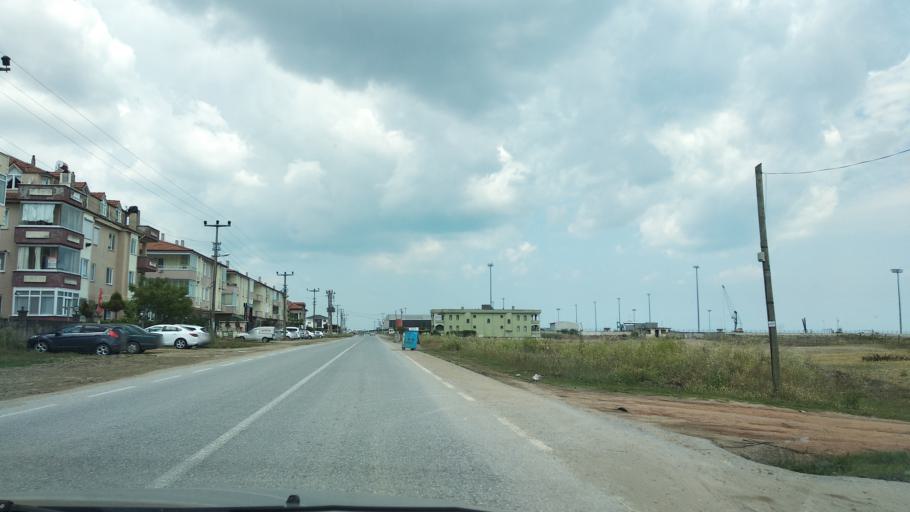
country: TR
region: Sakarya
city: Karasu
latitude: 41.1149
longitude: 30.6797
